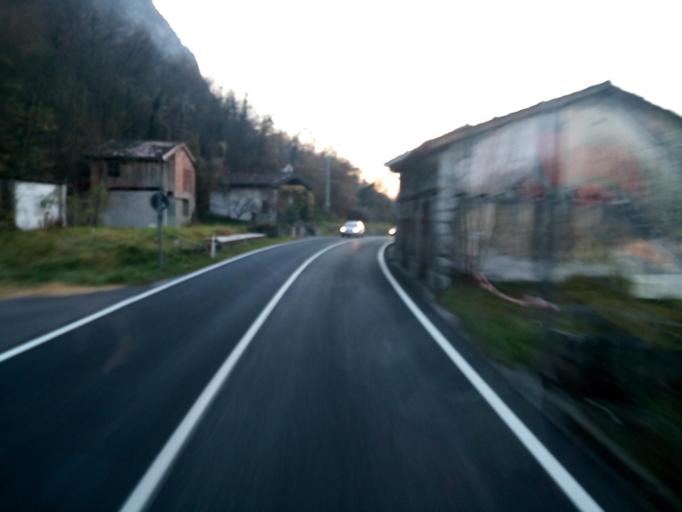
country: IT
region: Friuli Venezia Giulia
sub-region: Provincia di Udine
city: Villa Santina
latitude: 46.4154
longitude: 12.9295
